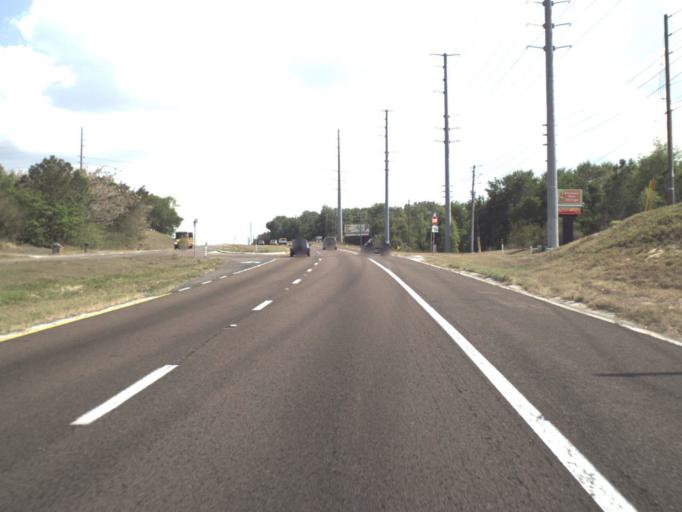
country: US
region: Florida
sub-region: Lake County
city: Minneola
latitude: 28.6114
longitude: -81.7587
